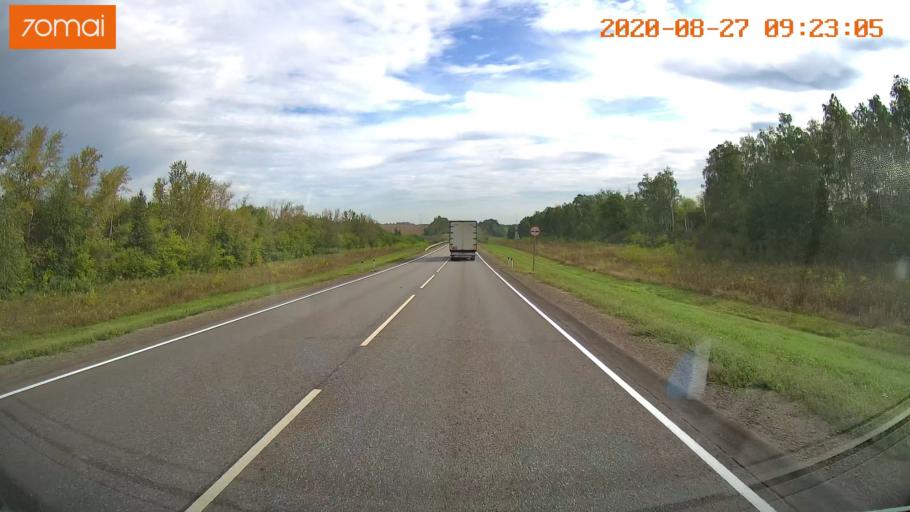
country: RU
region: Tula
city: Kazachka
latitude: 53.2712
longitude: 38.1571
